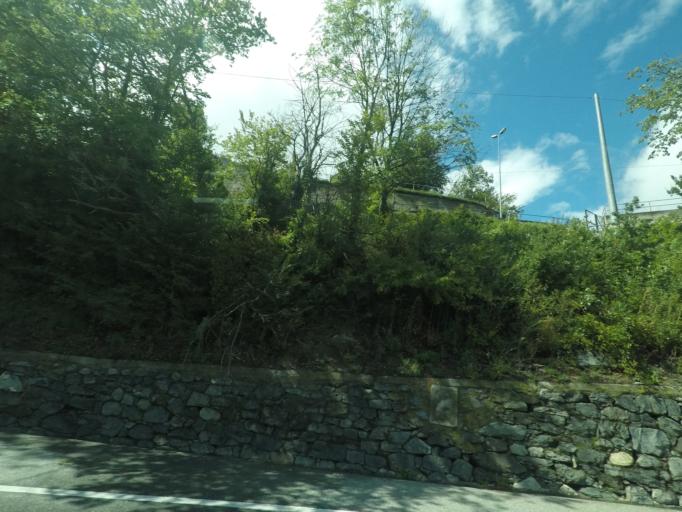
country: IT
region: Aosta Valley
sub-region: Valle d'Aosta
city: Chatillon
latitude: 45.7514
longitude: 7.6085
